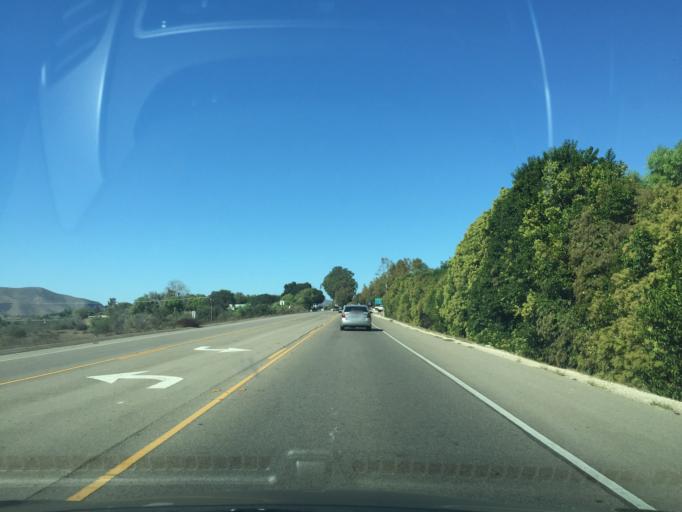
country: US
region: California
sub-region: Santa Barbara County
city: Buellton
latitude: 34.6073
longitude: -120.1777
